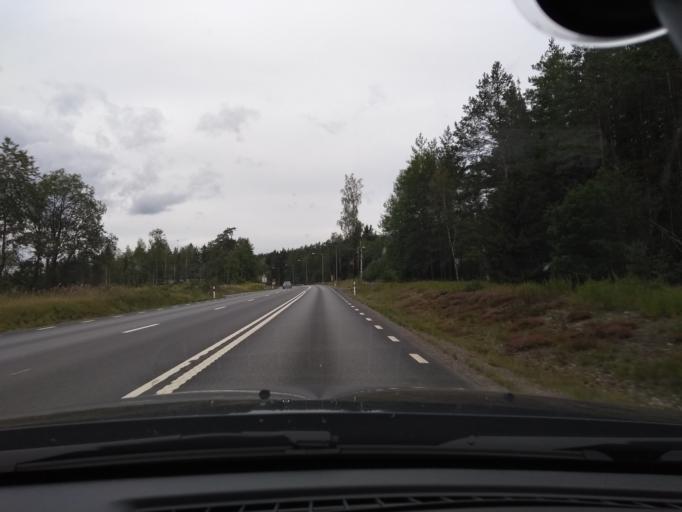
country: SE
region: Joenkoeping
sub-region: Eksjo Kommun
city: Haljarp
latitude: 57.6406
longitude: 15.2928
